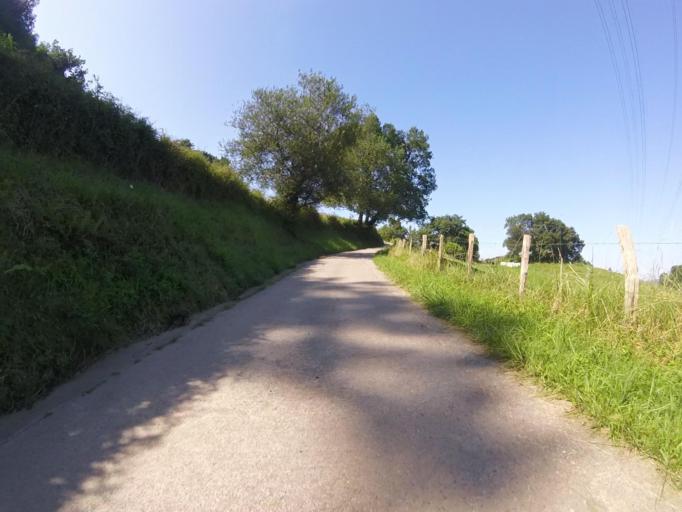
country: ES
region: Basque Country
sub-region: Provincia de Guipuzcoa
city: Astigarraga
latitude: 43.2732
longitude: -1.9185
